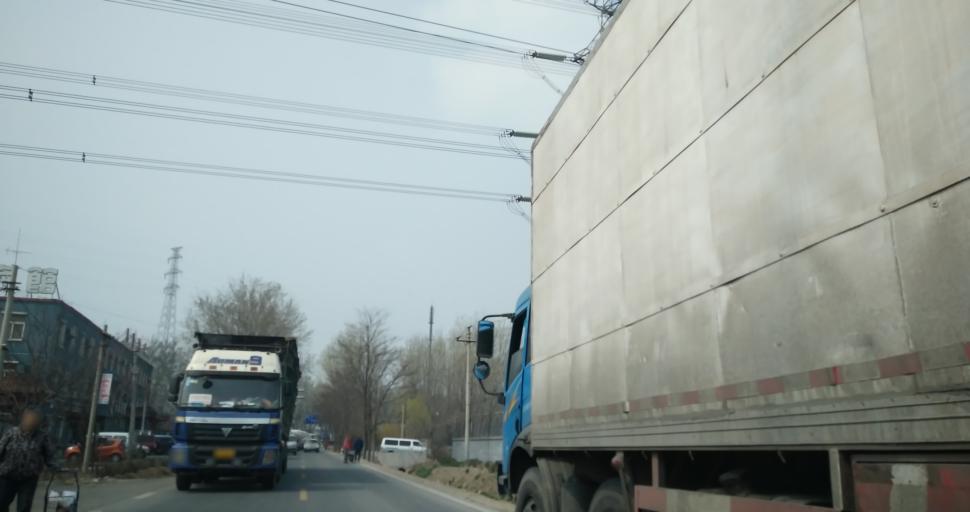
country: CN
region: Beijing
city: Qingyundian
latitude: 39.6899
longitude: 116.4915
